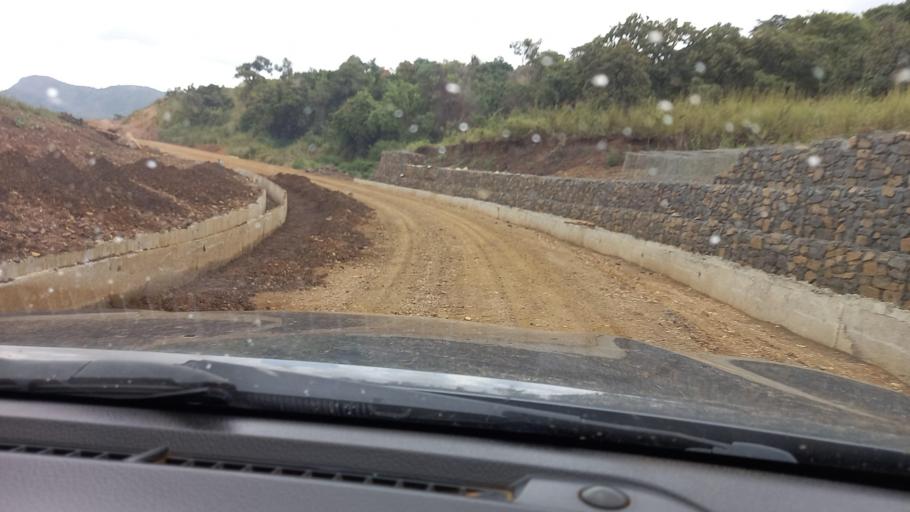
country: ET
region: Southern Nations, Nationalities, and People's Region
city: Mizan Teferi
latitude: 6.2082
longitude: 35.6686
